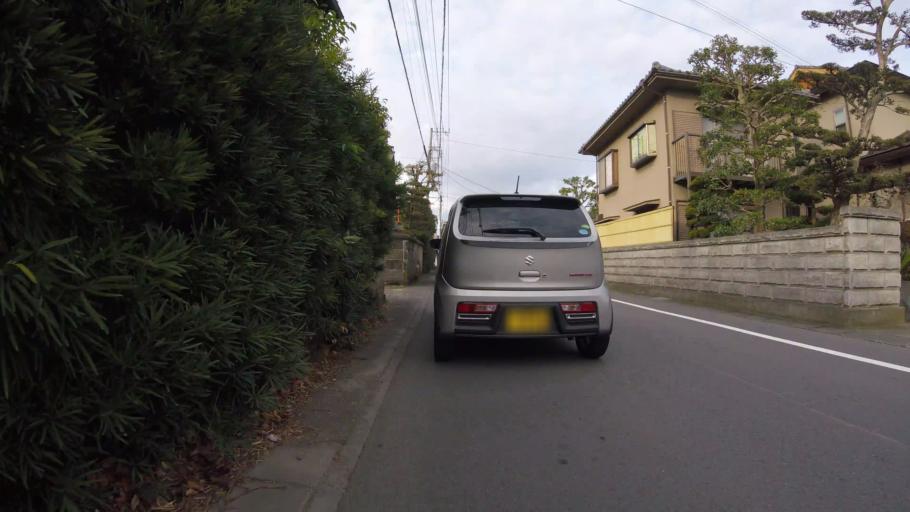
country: JP
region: Shizuoka
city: Mishima
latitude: 35.1068
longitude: 138.9113
